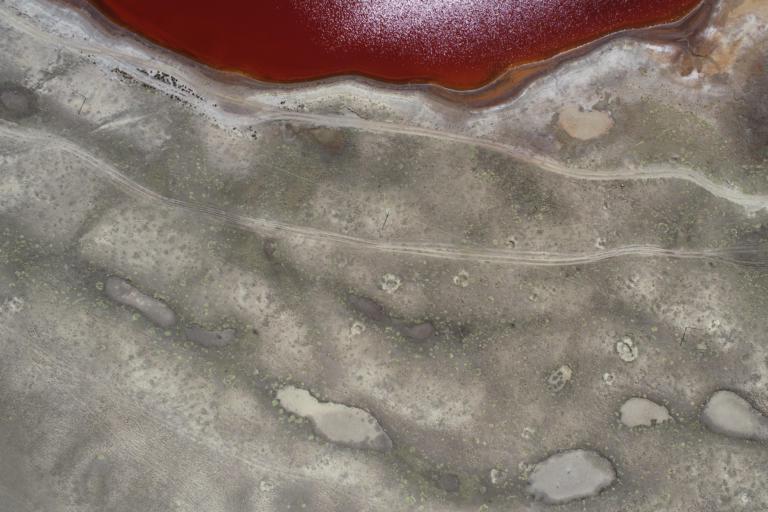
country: BO
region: La Paz
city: La Paz
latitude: -16.3441
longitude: -68.1614
